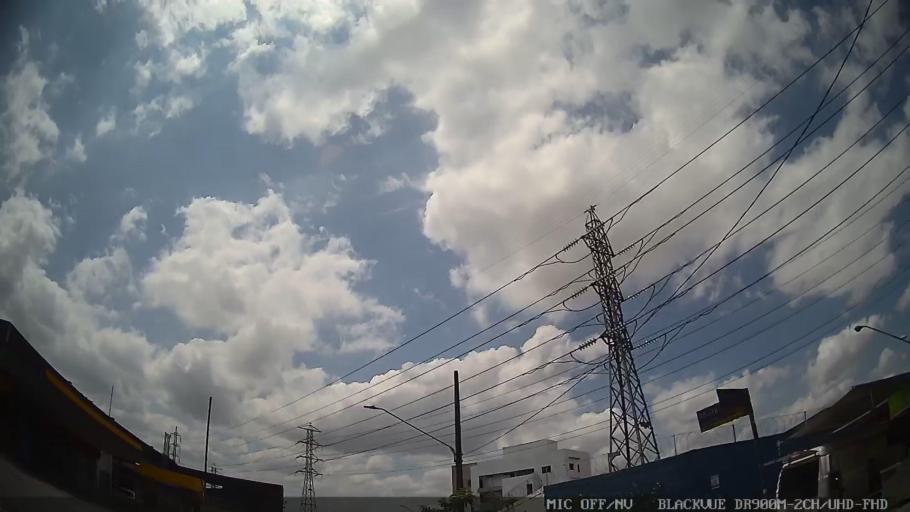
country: BR
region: Sao Paulo
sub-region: Guarulhos
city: Guarulhos
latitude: -23.5234
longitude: -46.5127
